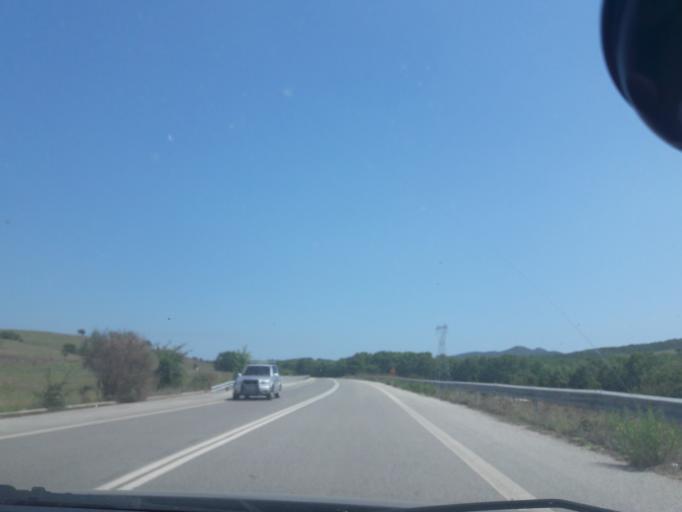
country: GR
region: Central Macedonia
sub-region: Nomos Chalkidikis
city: Megali Panagia
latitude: 40.3714
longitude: 23.6427
